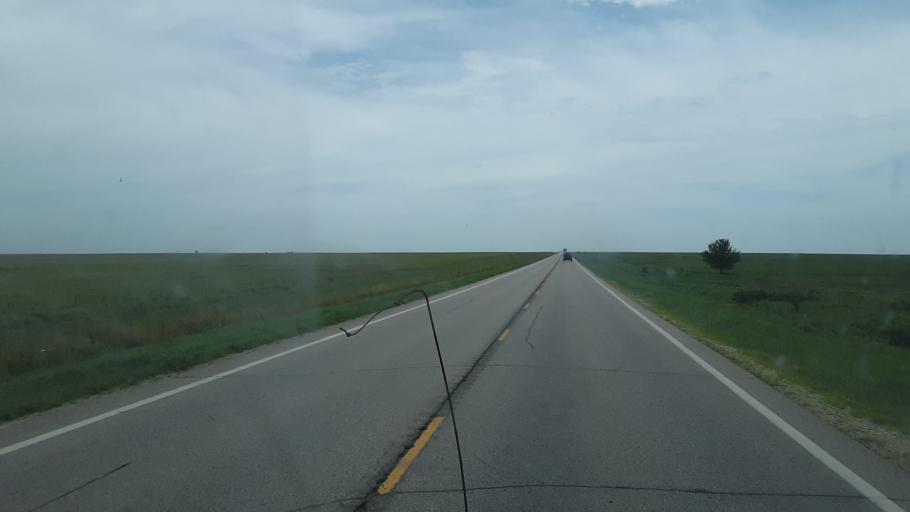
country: US
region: Kansas
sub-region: Butler County
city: El Dorado
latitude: 37.8102
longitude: -96.5967
